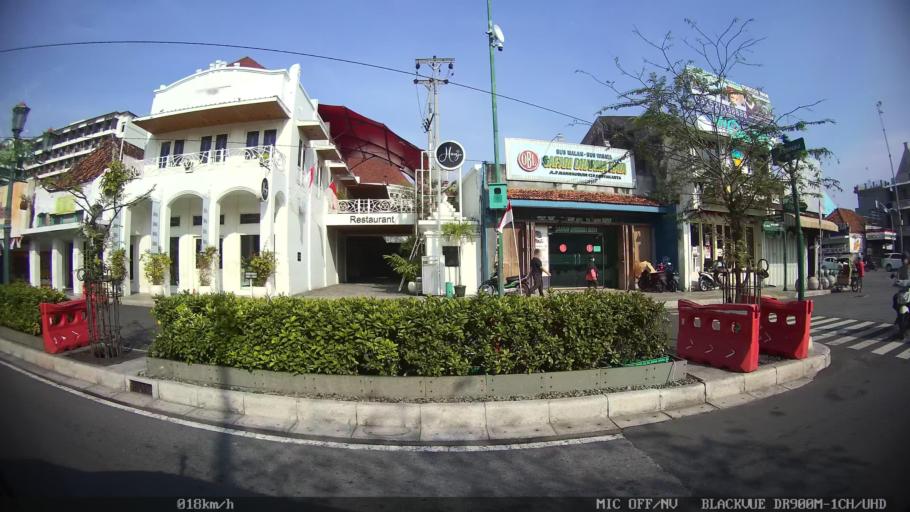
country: ID
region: Daerah Istimewa Yogyakarta
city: Yogyakarta
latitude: -7.7832
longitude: 110.3673
